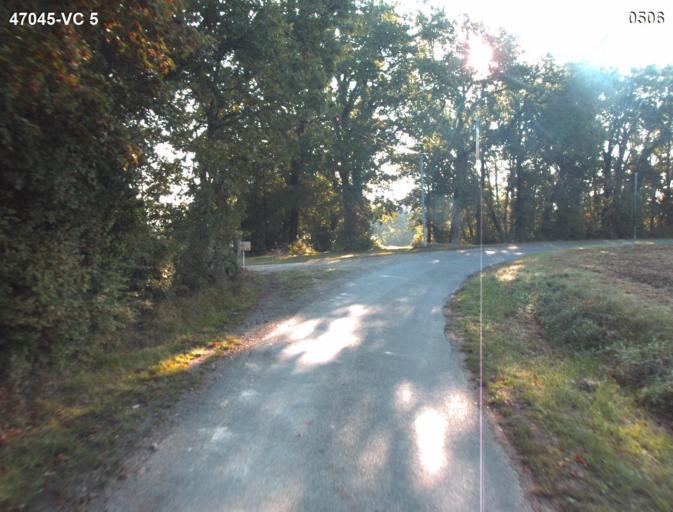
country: FR
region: Aquitaine
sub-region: Departement du Lot-et-Garonne
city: Nerac
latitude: 44.1367
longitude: 0.4107
